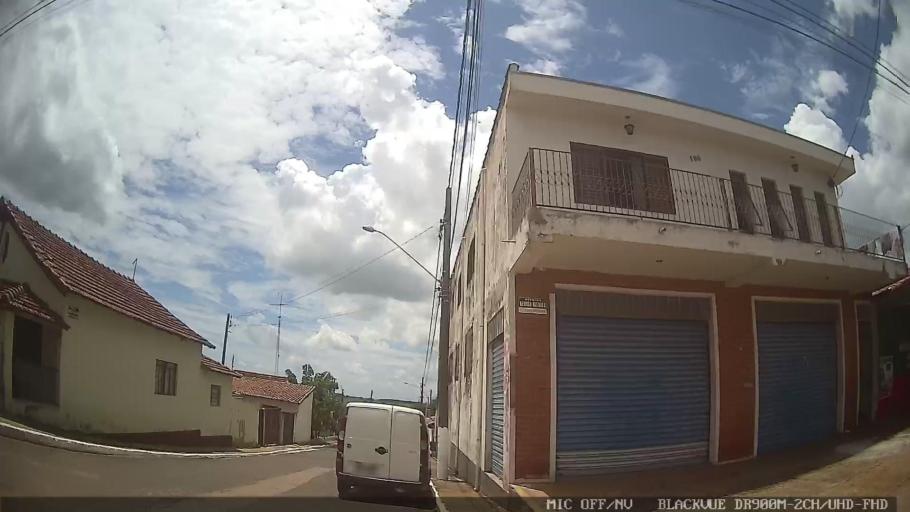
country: BR
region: Sao Paulo
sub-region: Laranjal Paulista
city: Laranjal Paulista
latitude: -23.0375
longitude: -47.8870
